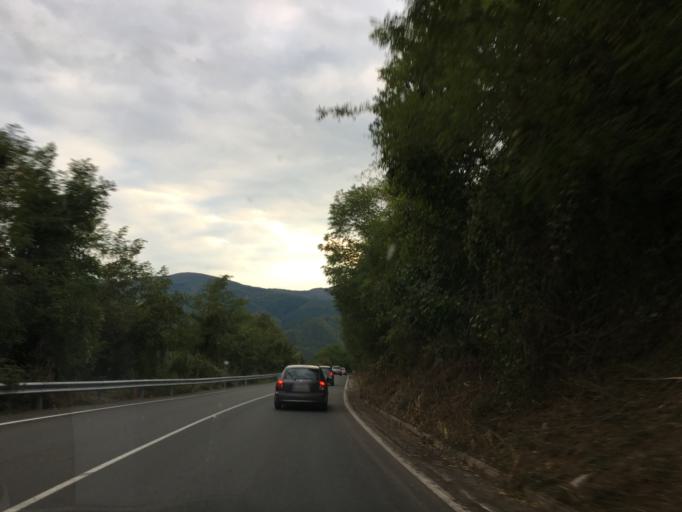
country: BG
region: Sofiya
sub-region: Obshtina Svoge
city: Svoge
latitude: 42.9708
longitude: 23.3523
